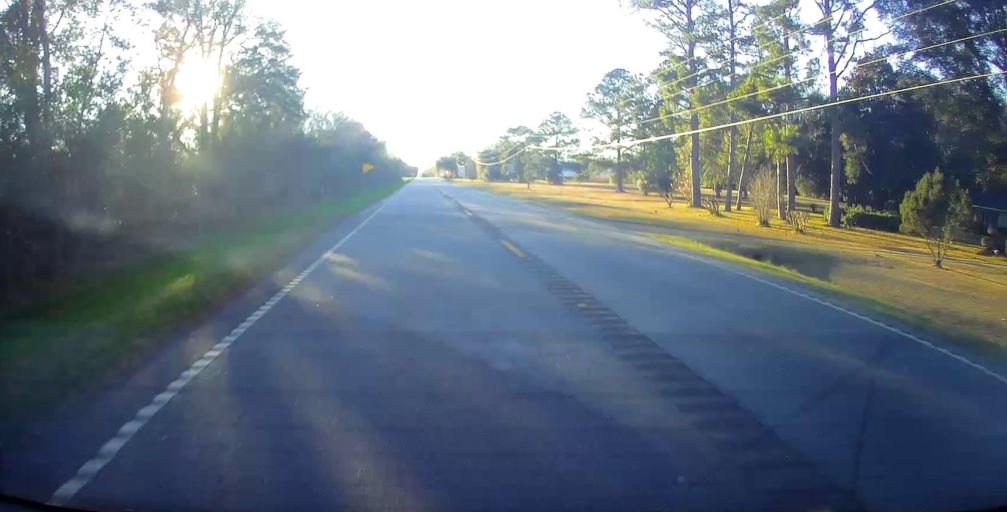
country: US
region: Georgia
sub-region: Dougherty County
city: Albany
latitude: 31.5041
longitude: -84.2382
